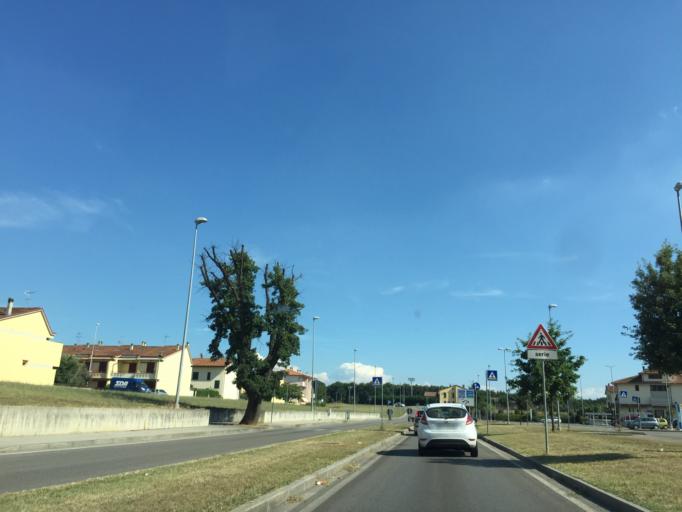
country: IT
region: Tuscany
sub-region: Provincia di Pistoia
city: San Rocco
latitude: 43.8207
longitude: 10.8736
